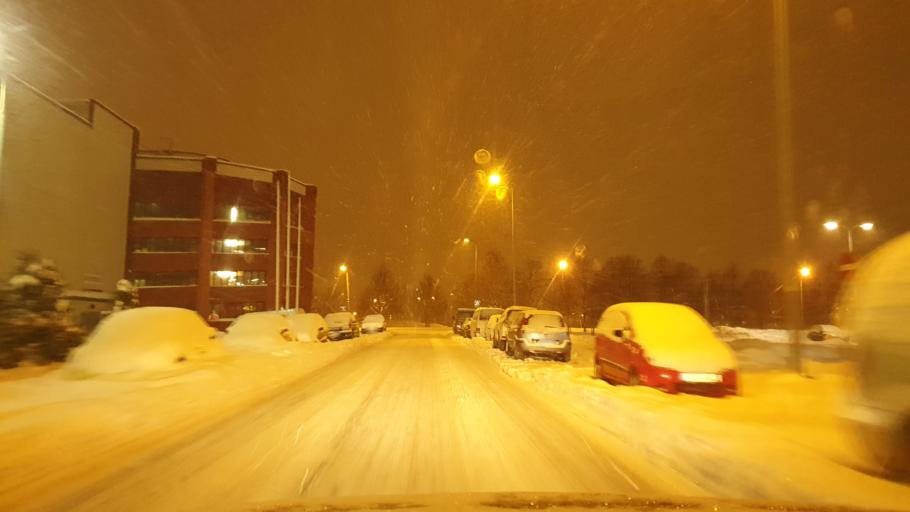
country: EE
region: Harju
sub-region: Tallinna linn
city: Kose
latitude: 59.4450
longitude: 24.8819
